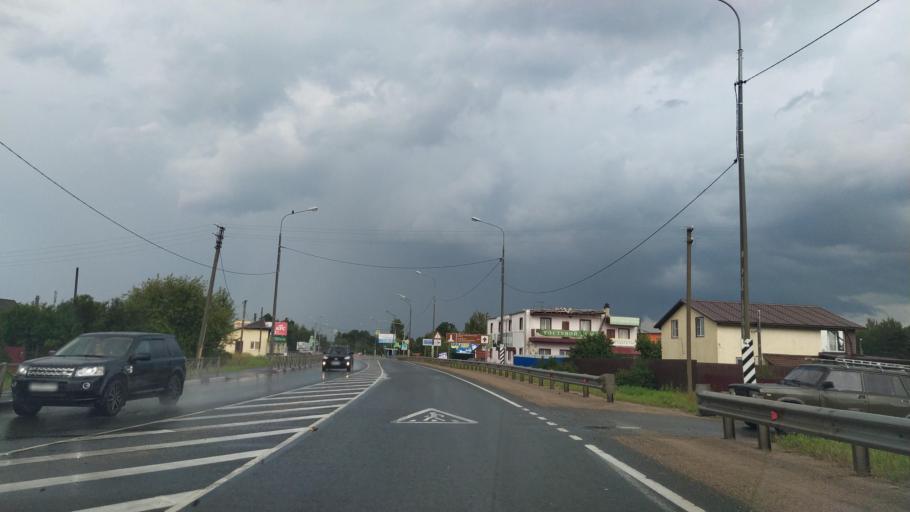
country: RU
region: Pskov
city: Pskov
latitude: 57.7433
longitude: 28.3696
